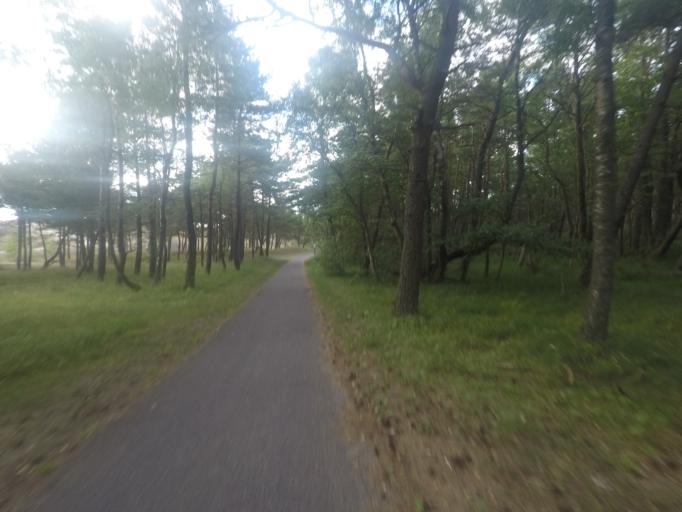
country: LT
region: Klaipedos apskritis
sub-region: Klaipeda
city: Klaipeda
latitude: 55.6529
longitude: 21.1078
